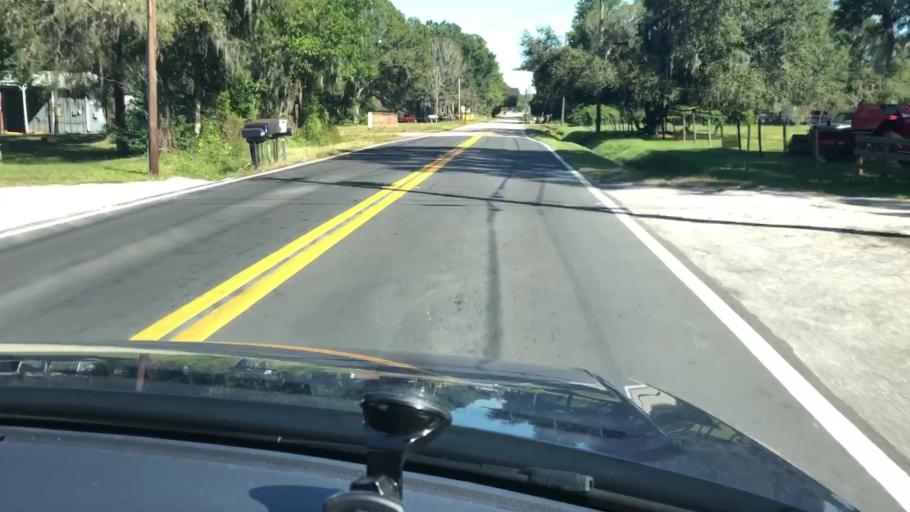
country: US
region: Florida
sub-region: Polk County
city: Gibsonia
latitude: 28.1354
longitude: -81.9799
